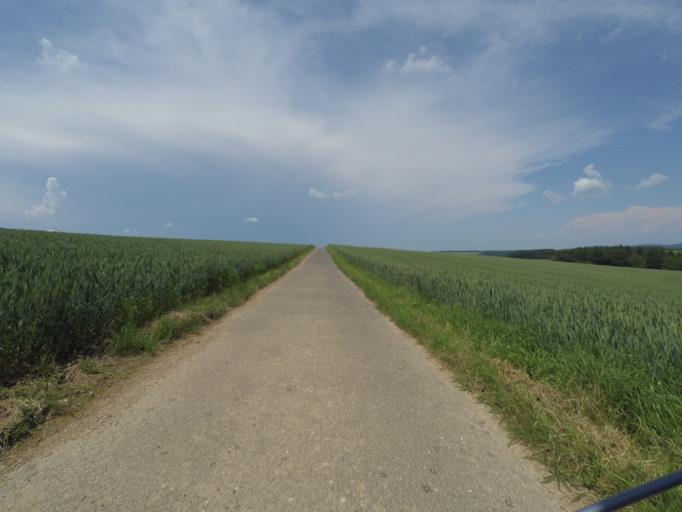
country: DE
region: Rheinland-Pfalz
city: Mermuth
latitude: 50.1647
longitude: 7.4706
